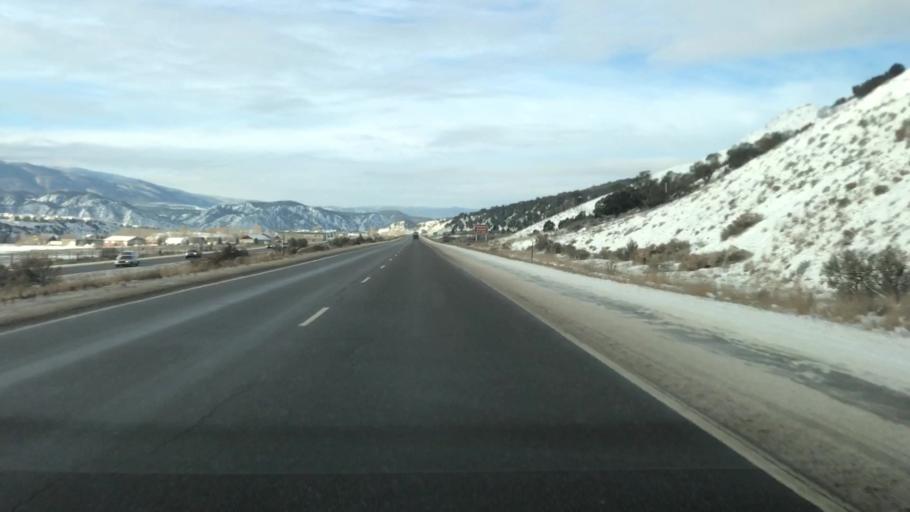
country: US
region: Colorado
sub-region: Eagle County
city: Eagle
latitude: 39.6705
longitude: -106.8029
